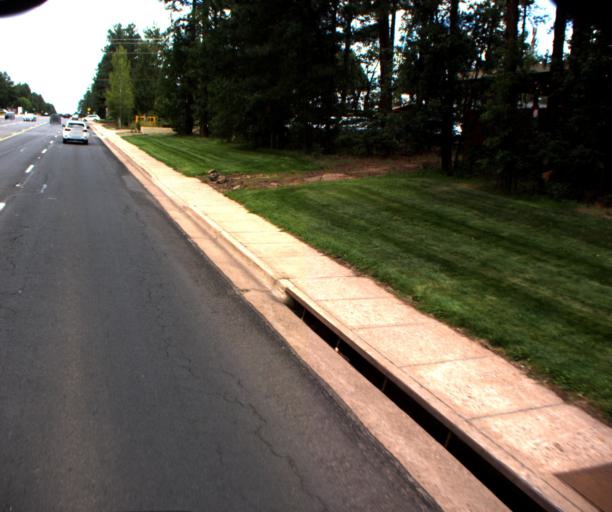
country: US
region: Arizona
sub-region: Navajo County
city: Pinetop-Lakeside
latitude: 34.1374
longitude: -109.9514
